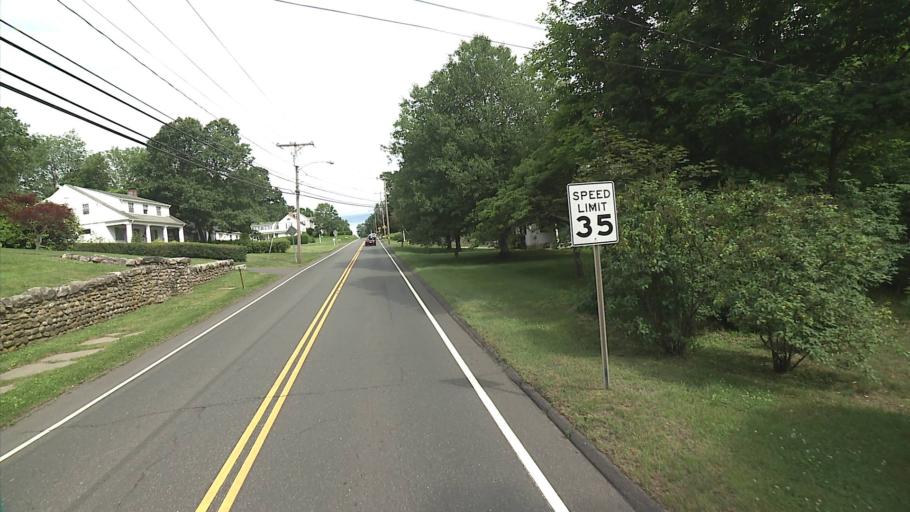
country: US
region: Connecticut
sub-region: Litchfield County
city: Watertown
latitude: 41.6098
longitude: -73.1213
